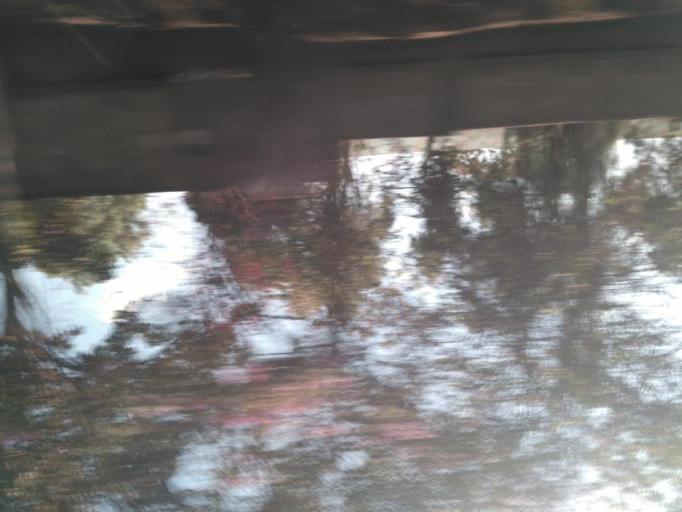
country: TZ
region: Arusha
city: Arusha
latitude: -3.3695
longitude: 36.6899
